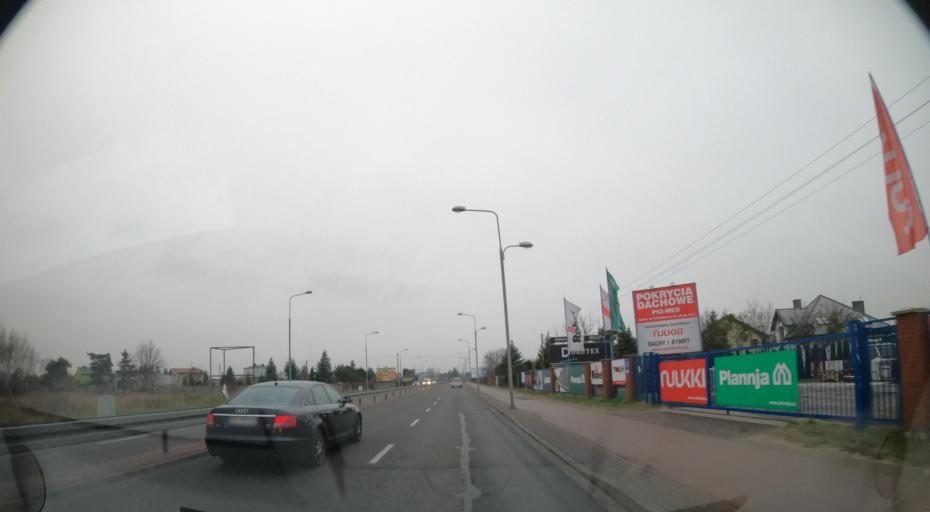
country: PL
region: Masovian Voivodeship
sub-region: Radom
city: Radom
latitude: 51.4215
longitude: 21.2129
